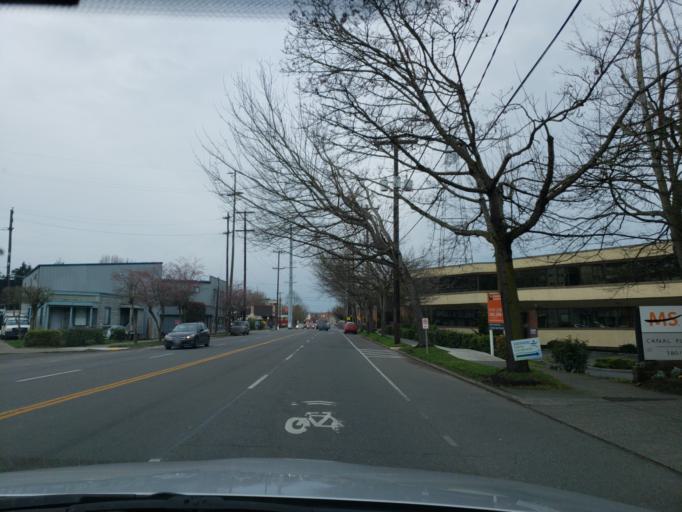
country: US
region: Washington
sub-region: King County
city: Seattle
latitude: 47.6478
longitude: -122.3533
